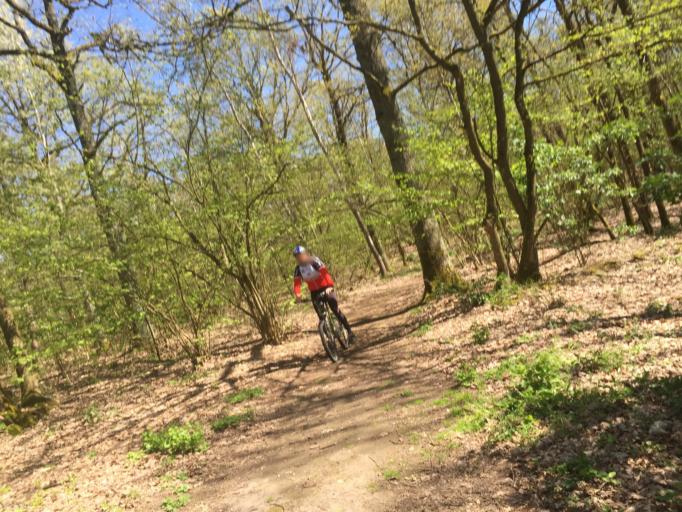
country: DE
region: Bavaria
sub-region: Regierungsbezirk Unterfranken
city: Sulzfeld
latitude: 50.2736
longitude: 10.4127
